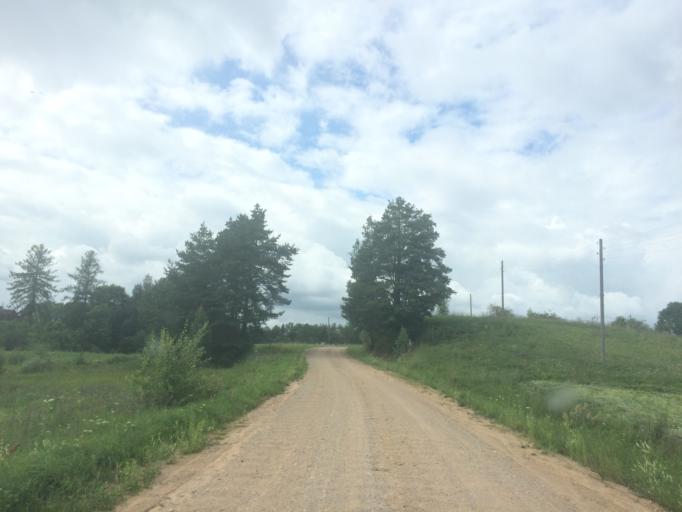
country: LV
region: Rezekne
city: Rezekne
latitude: 56.6584
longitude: 27.2720
